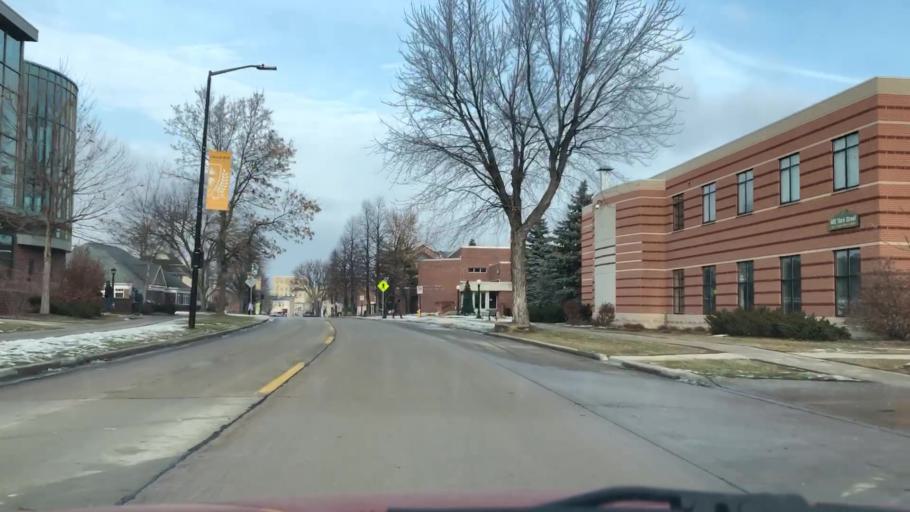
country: US
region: Wisconsin
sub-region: Brown County
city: De Pere
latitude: 44.4436
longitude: -88.0687
